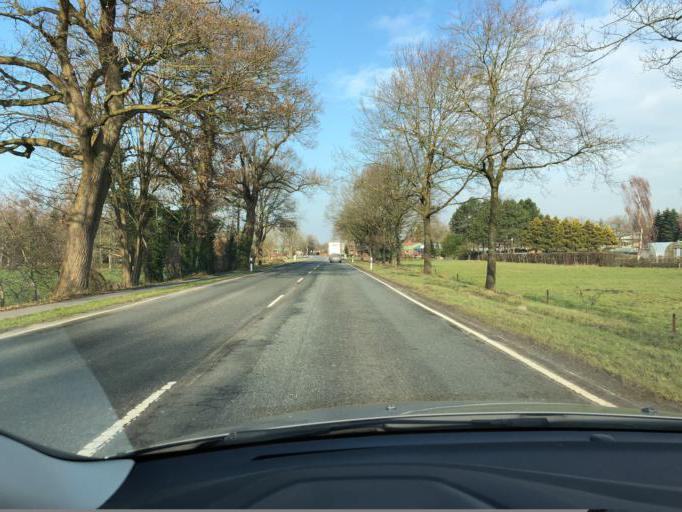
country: DE
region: Lower Saxony
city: Westerstede
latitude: 53.2836
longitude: 7.8986
